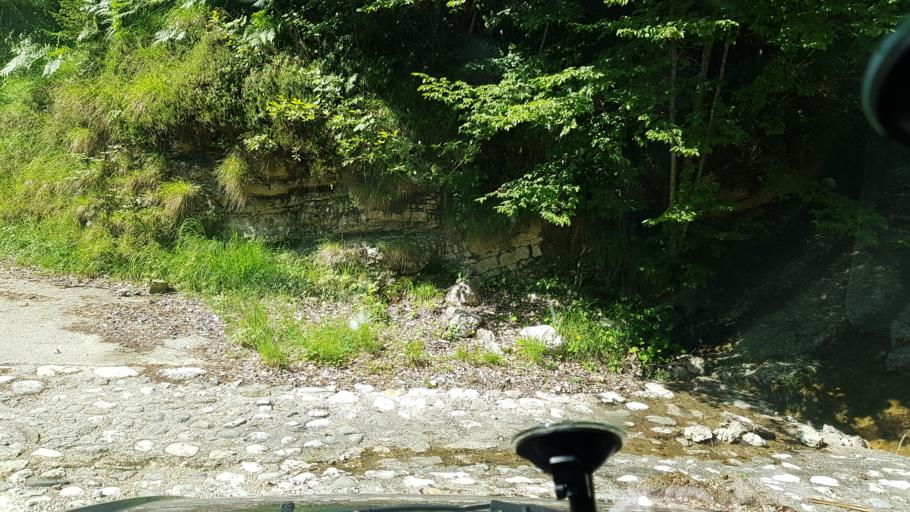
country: IT
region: Friuli Venezia Giulia
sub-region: Provincia di Udine
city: Dogna
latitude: 46.4414
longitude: 13.2973
